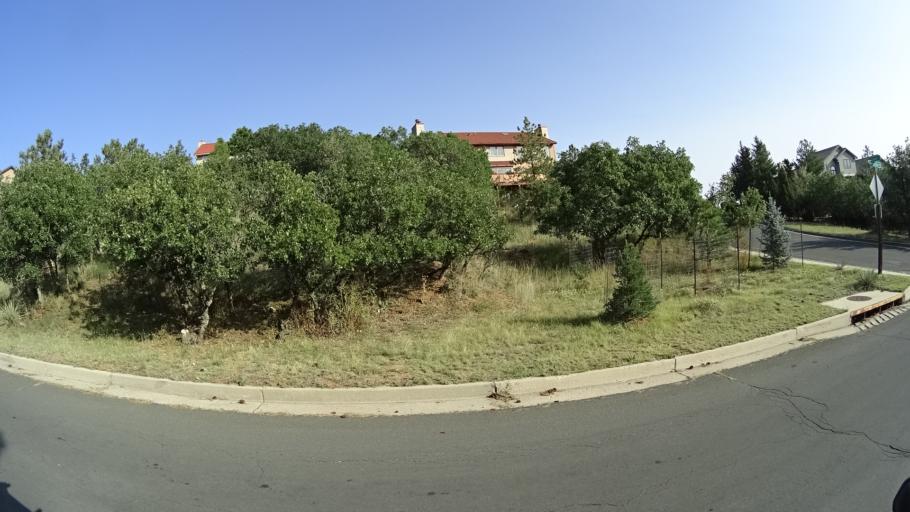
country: US
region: Colorado
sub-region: El Paso County
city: Colorado Springs
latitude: 38.8234
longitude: -104.8740
